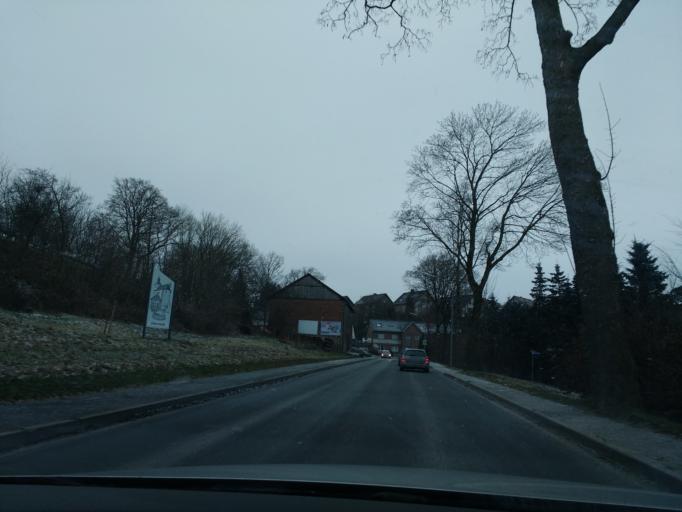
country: DE
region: North Rhine-Westphalia
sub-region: Regierungsbezirk Detmold
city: Wunnenberg
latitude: 51.5186
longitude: 8.6945
